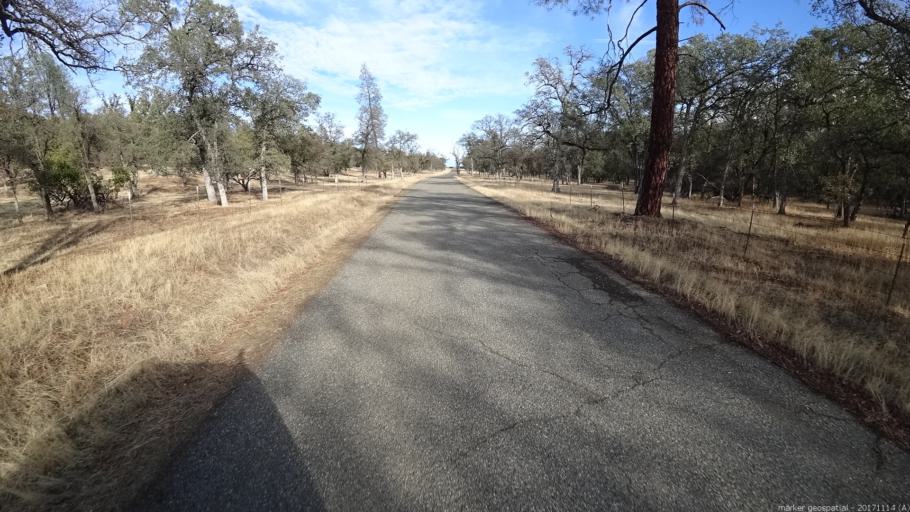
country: US
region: California
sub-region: Shasta County
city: Shasta
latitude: 40.3825
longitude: -122.5619
